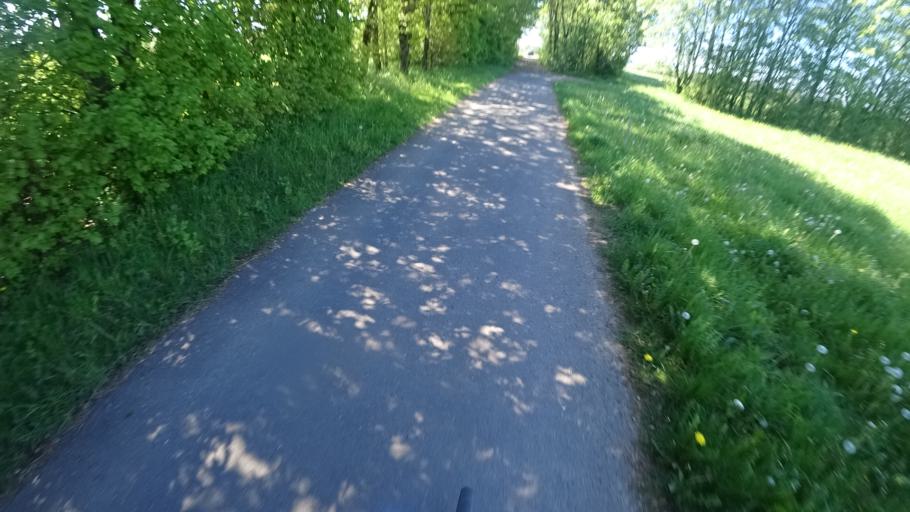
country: DE
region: Rheinland-Pfalz
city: Neunkhausen
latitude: 50.7197
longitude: 7.9029
